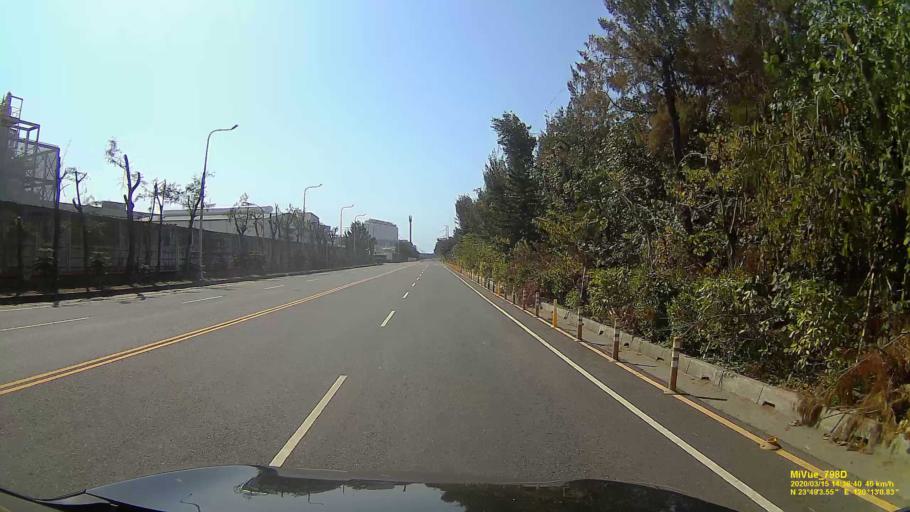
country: TW
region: Taiwan
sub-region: Yunlin
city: Douliu
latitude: 23.8177
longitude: 120.2167
